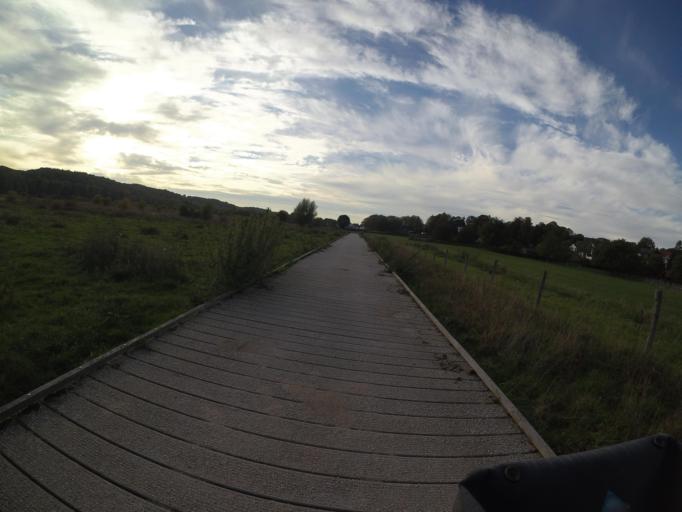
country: NL
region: Limburg
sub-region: Valkenburg aan de Geul
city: Broekhem
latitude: 50.8704
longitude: 5.8107
